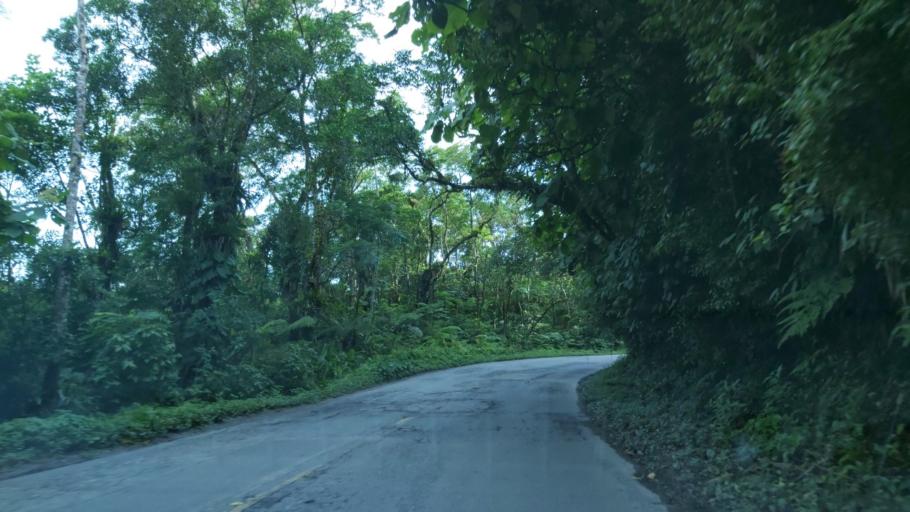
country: BR
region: Sao Paulo
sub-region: Miracatu
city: Miracatu
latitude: -24.0364
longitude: -47.5667
